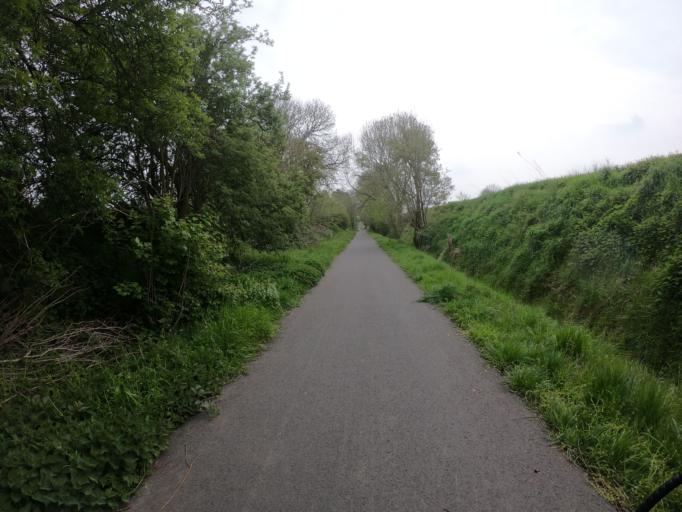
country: BE
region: Flanders
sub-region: Provincie West-Vlaanderen
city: Avelgem
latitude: 50.7733
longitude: 3.4322
